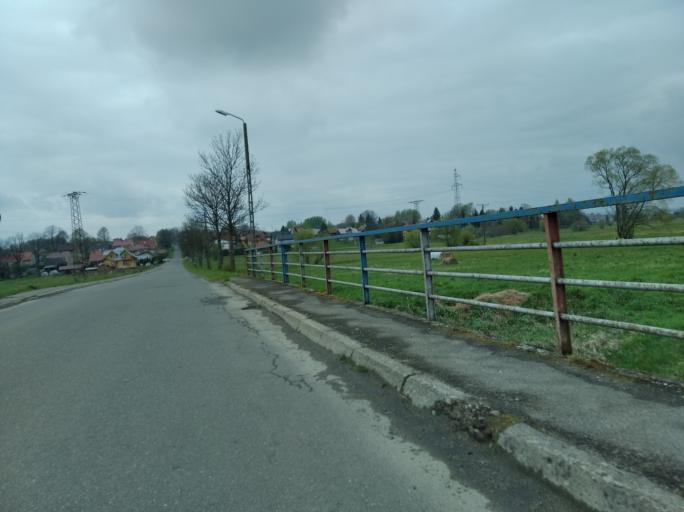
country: PL
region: Subcarpathian Voivodeship
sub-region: Powiat brzozowski
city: Stara Wies
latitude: 49.7140
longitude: 22.0101
